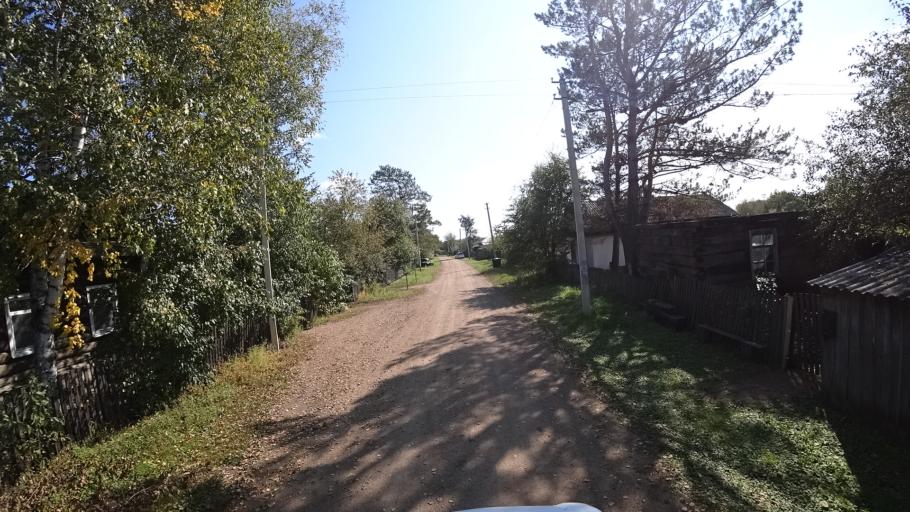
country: RU
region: Amur
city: Arkhara
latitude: 49.4014
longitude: 130.1495
